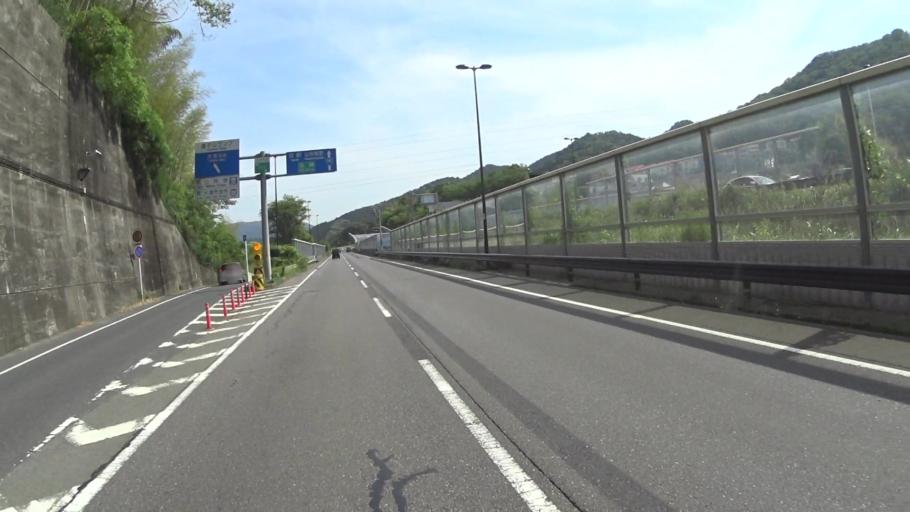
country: JP
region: Shiga Prefecture
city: Otsu-shi
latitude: 35.0305
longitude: 135.8501
